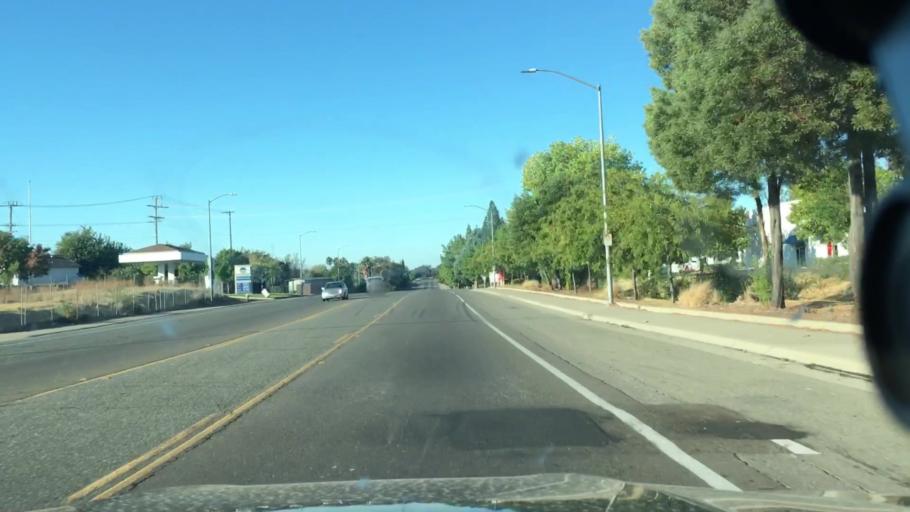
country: US
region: California
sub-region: Sacramento County
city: Antelope
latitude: 38.6982
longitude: -121.3356
